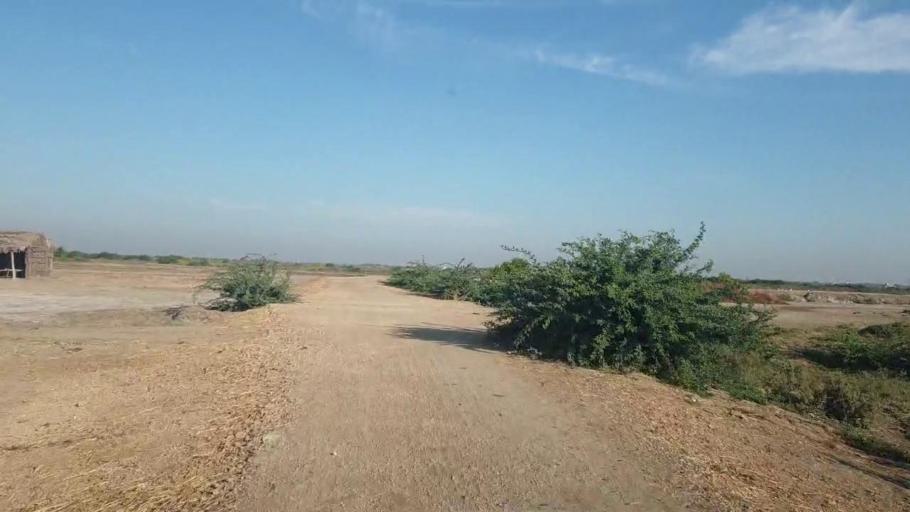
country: PK
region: Sindh
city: Talhar
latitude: 24.8321
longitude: 68.8388
